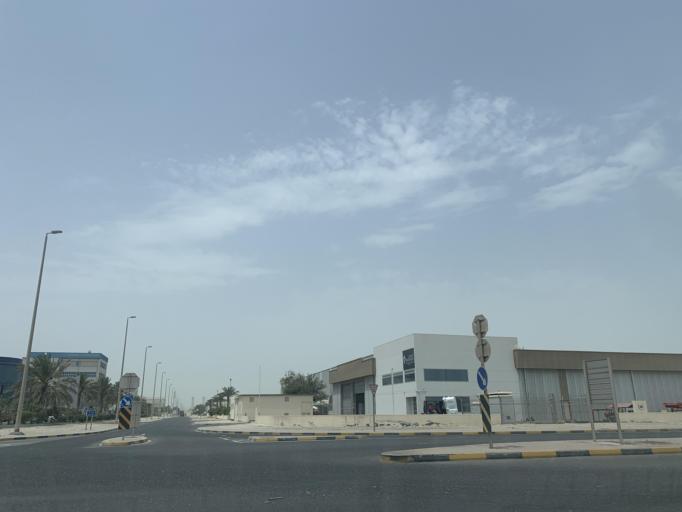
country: BH
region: Muharraq
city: Al Hadd
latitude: 26.2182
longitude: 50.6796
